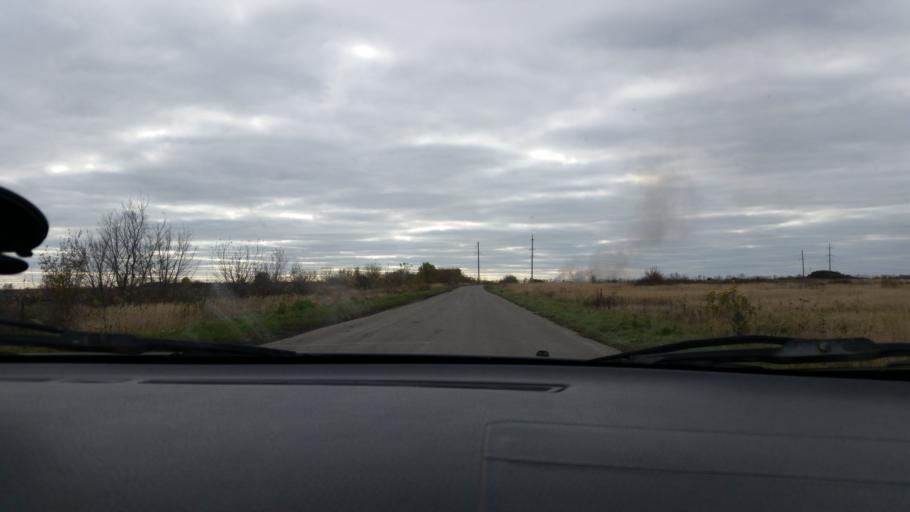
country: RU
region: Lipetsk
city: Gryazi
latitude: 52.4655
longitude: 39.9337
